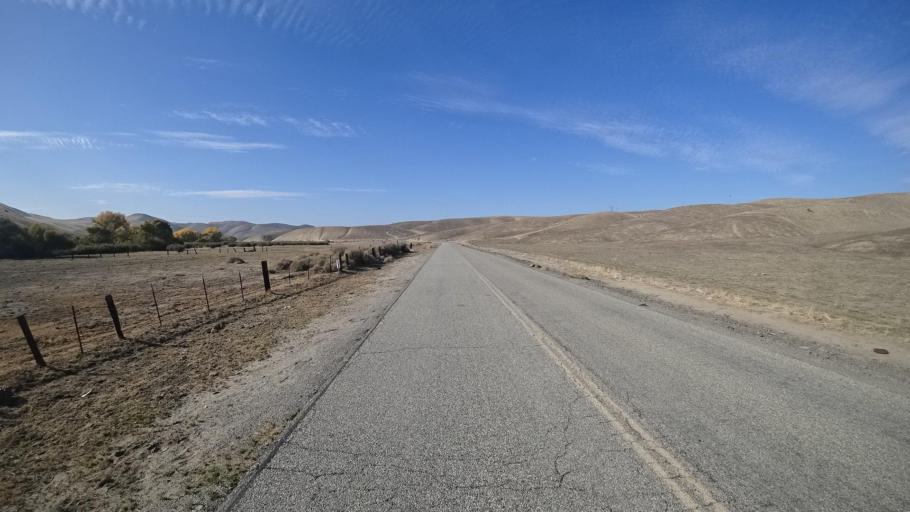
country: US
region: California
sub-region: Kern County
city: Oildale
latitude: 35.5167
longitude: -118.9130
